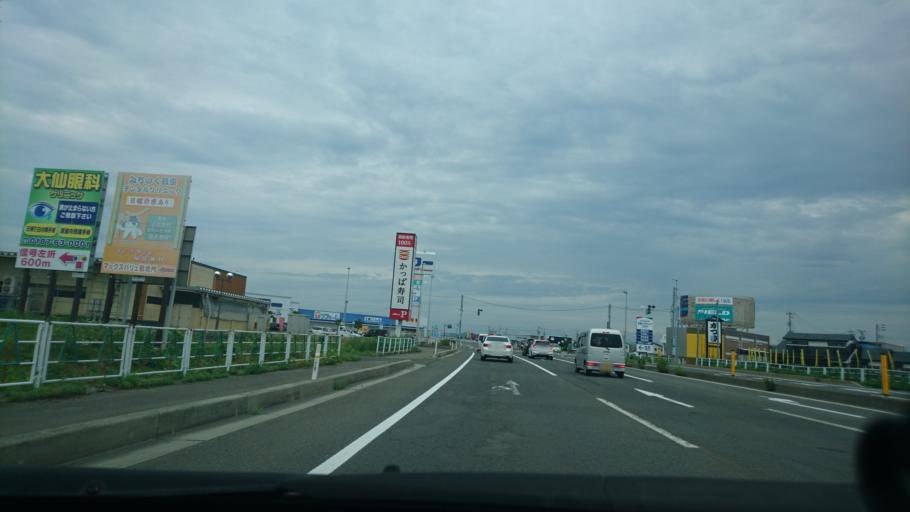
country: JP
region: Akita
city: Omagari
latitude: 39.4697
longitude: 140.4861
